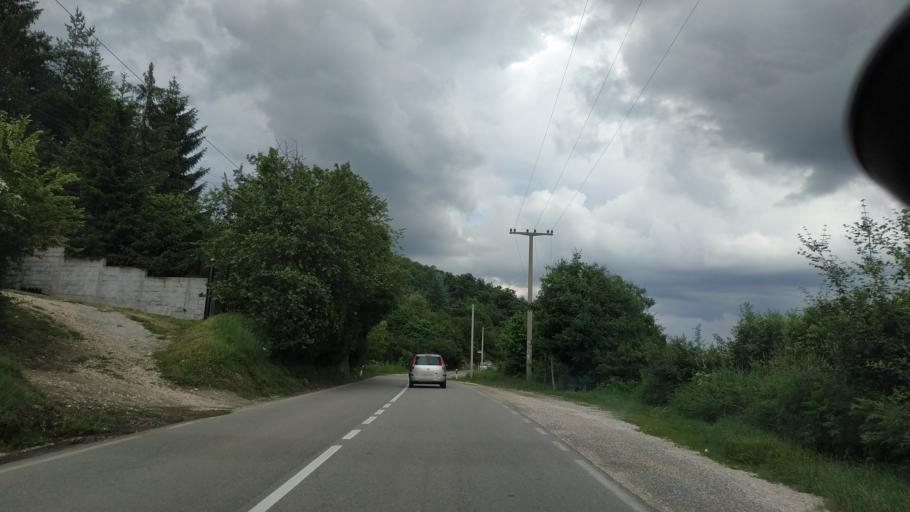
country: RS
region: Central Serbia
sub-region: Borski Okrug
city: Bor
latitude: 44.0509
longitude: 22.0732
